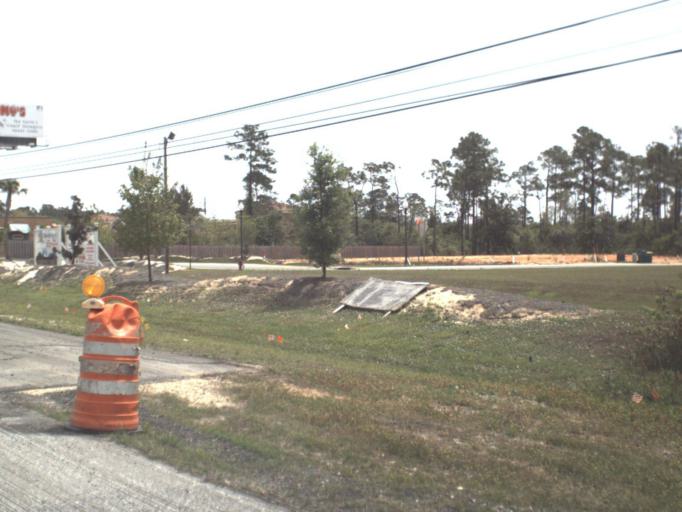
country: US
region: Florida
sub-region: Santa Rosa County
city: Holley
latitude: 30.4020
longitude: -86.9200
